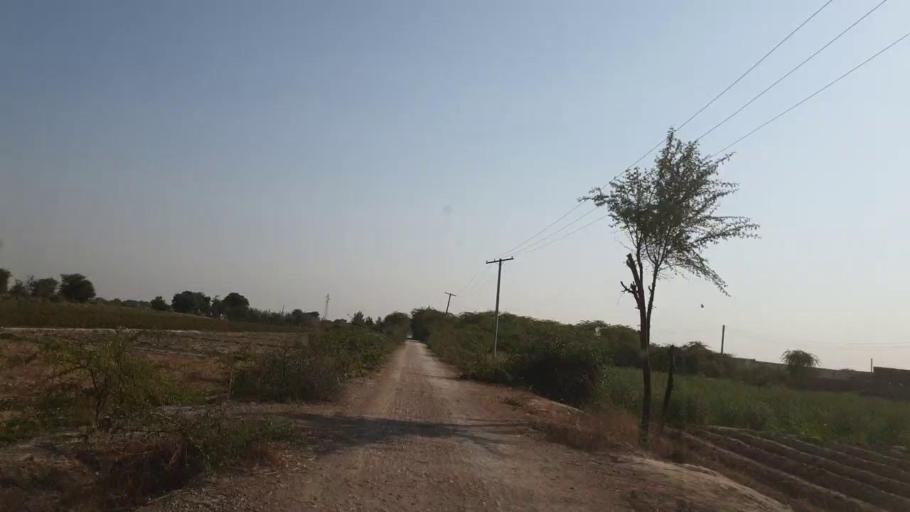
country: PK
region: Sindh
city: Naukot
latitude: 25.0216
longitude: 69.4696
